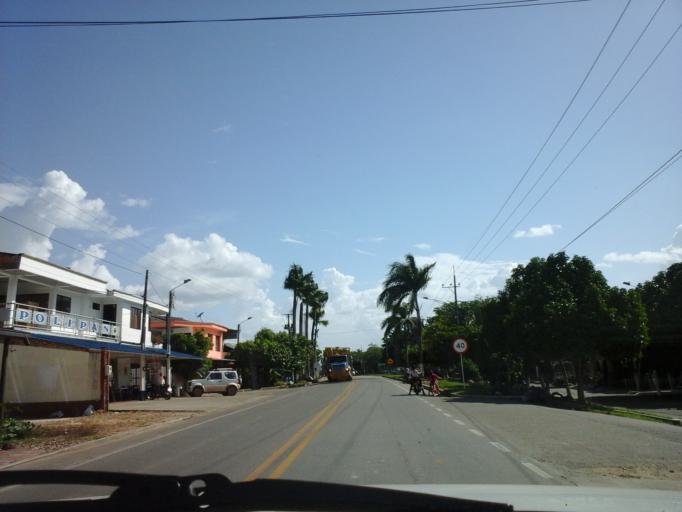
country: CO
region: Meta
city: Puerto Lopez
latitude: 4.0920
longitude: -72.9553
